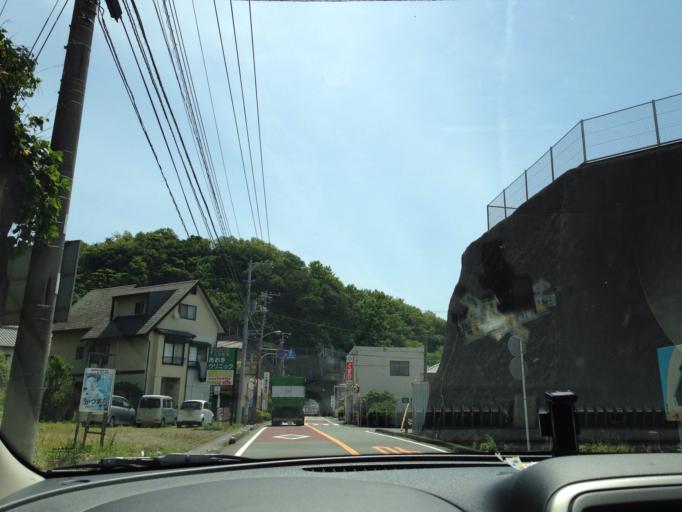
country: JP
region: Shizuoka
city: Numazu
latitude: 35.0514
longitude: 138.8979
